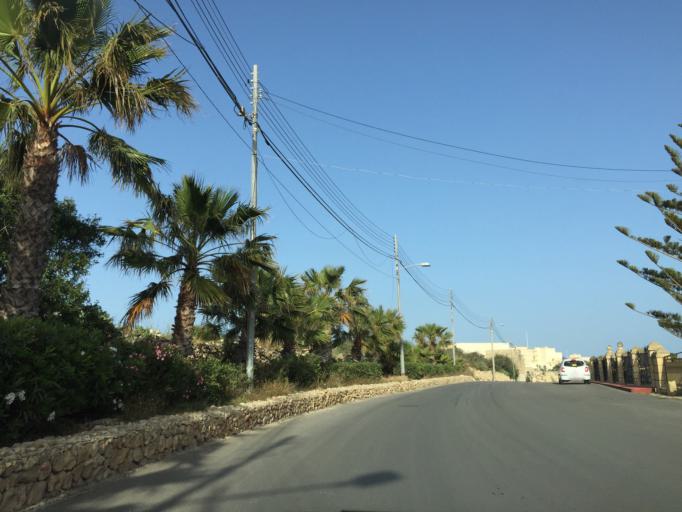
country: MT
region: Il-Qala
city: Qala
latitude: 36.0360
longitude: 14.3168
